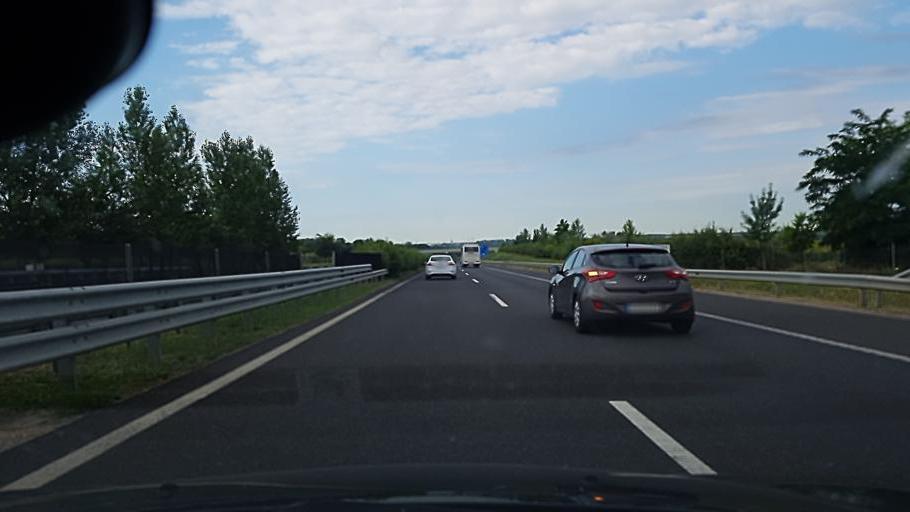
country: HU
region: Pest
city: Szazhalombatta
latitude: 47.3548
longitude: 18.9032
